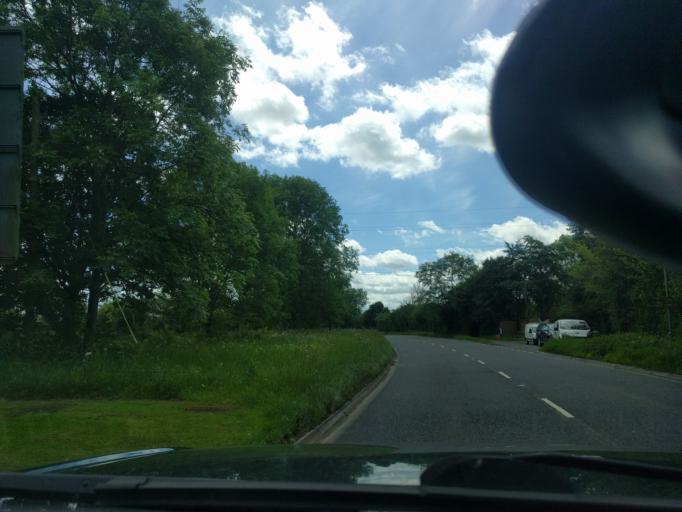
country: GB
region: England
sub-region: Wiltshire
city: Melksham
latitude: 51.3882
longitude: -2.1428
